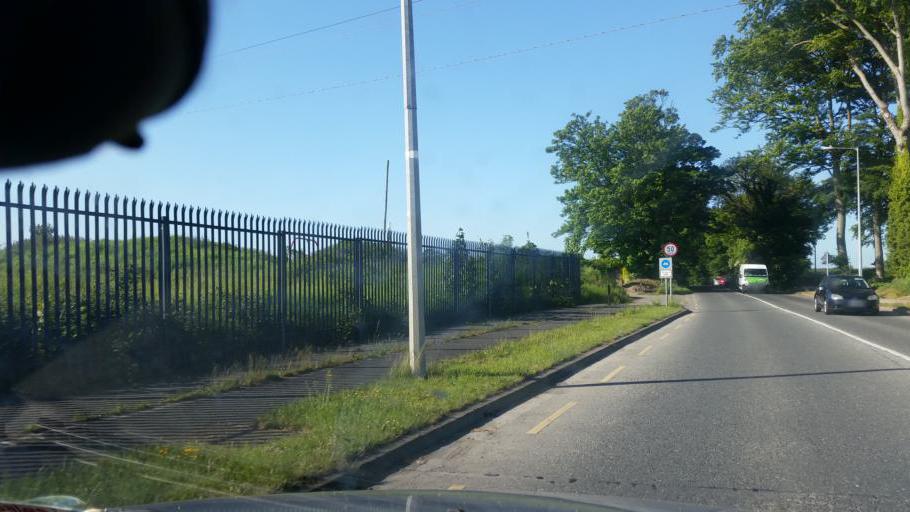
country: IE
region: Leinster
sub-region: Fingal County
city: Blanchardstown
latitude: 53.4133
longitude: -6.3873
